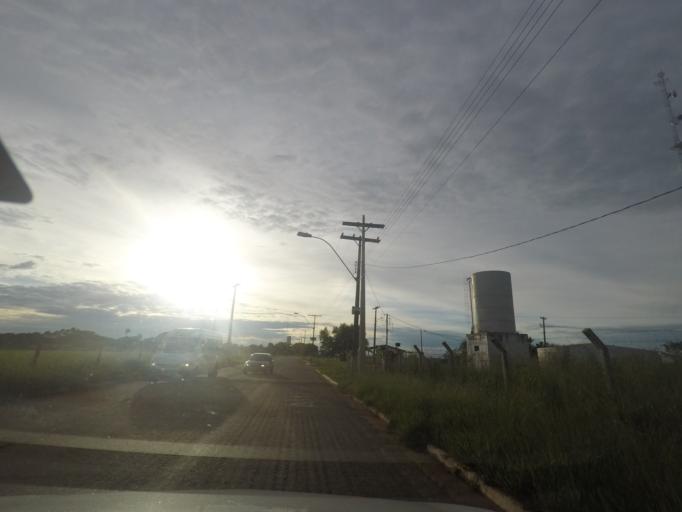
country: BR
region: Goias
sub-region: Trindade
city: Trindade
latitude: -16.7200
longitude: -49.4379
